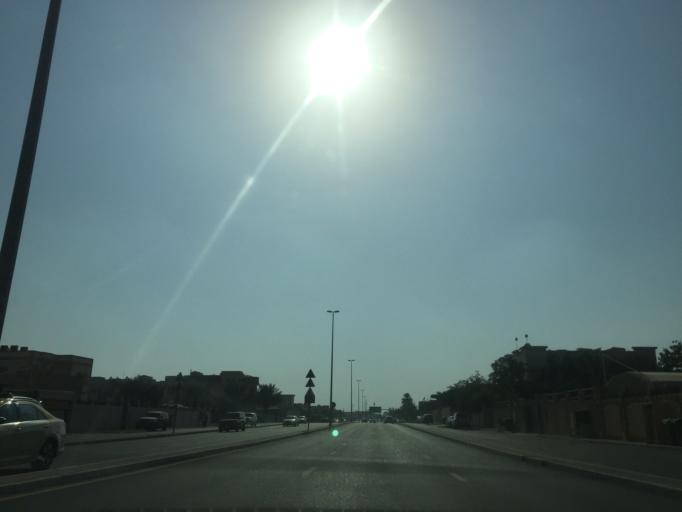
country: AE
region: Dubai
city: Dubai
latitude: 25.1057
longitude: 55.2163
